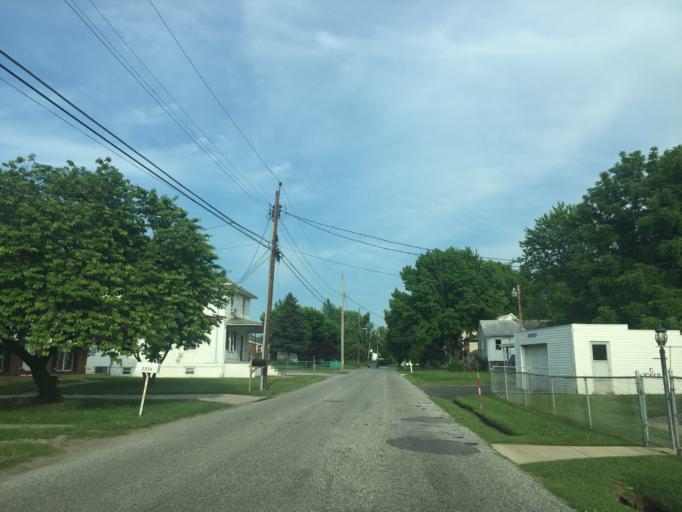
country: US
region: Maryland
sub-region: Baltimore County
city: Edgemere
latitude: 39.2350
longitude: -76.4540
